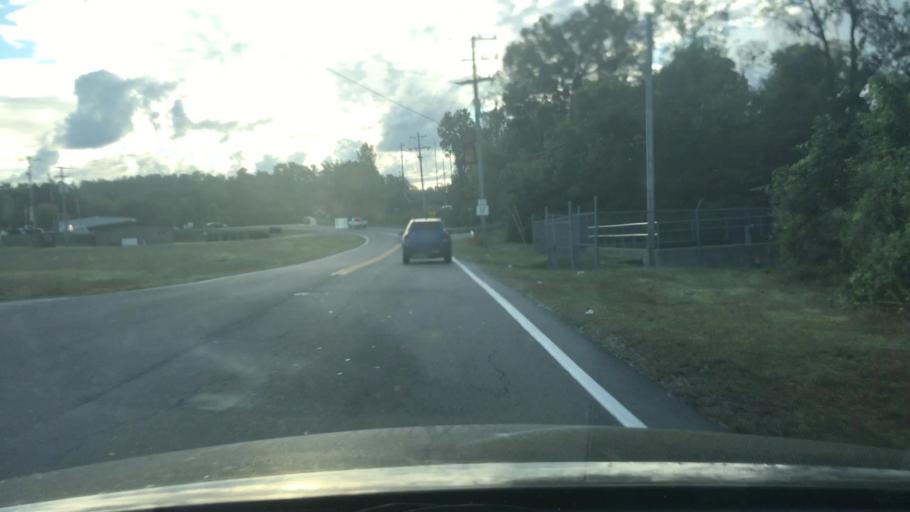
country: US
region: Tennessee
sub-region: Cheatham County
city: Ashland City
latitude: 36.2649
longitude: -87.0609
